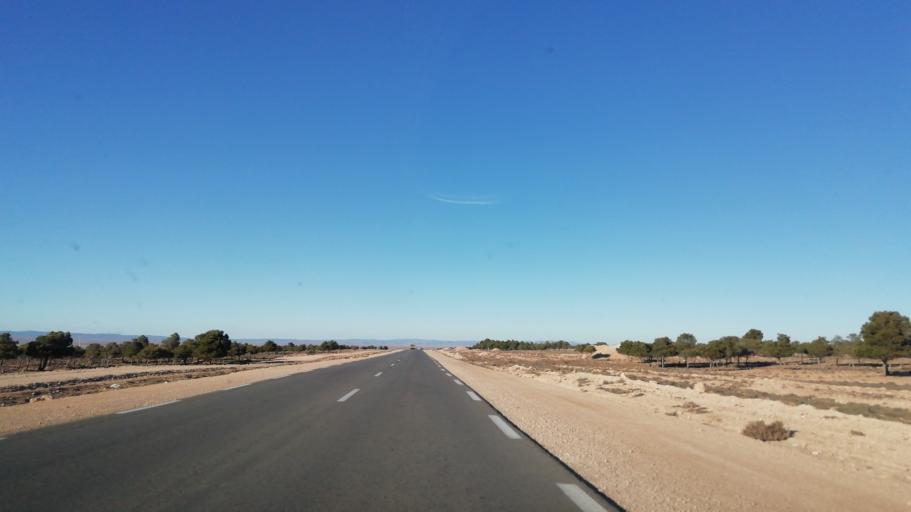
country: DZ
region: Tlemcen
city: Sebdou
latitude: 34.2848
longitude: -1.2595
